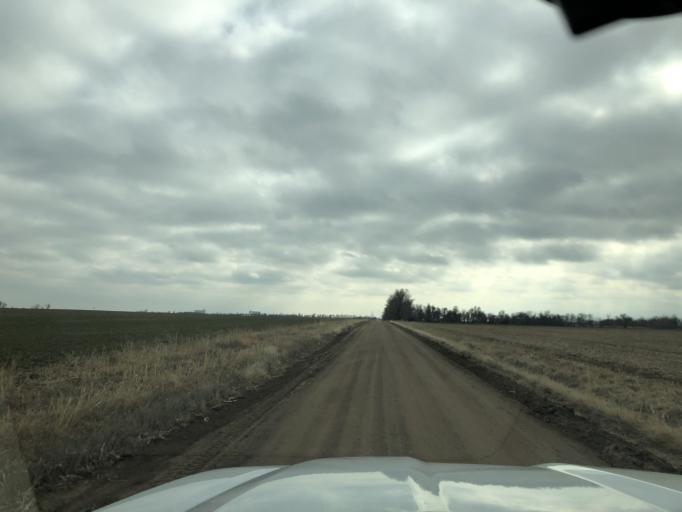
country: US
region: Kansas
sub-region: Reno County
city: Nickerson
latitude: 38.0090
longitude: -98.2158
